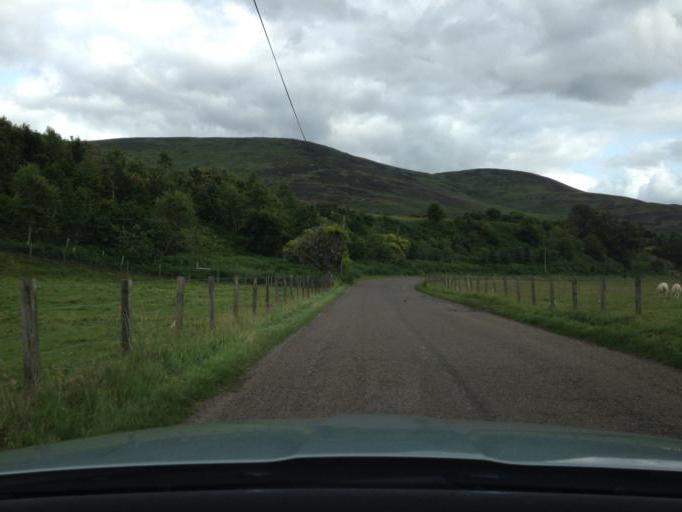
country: GB
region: Scotland
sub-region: Angus
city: Brechin
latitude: 56.8911
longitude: -2.7162
